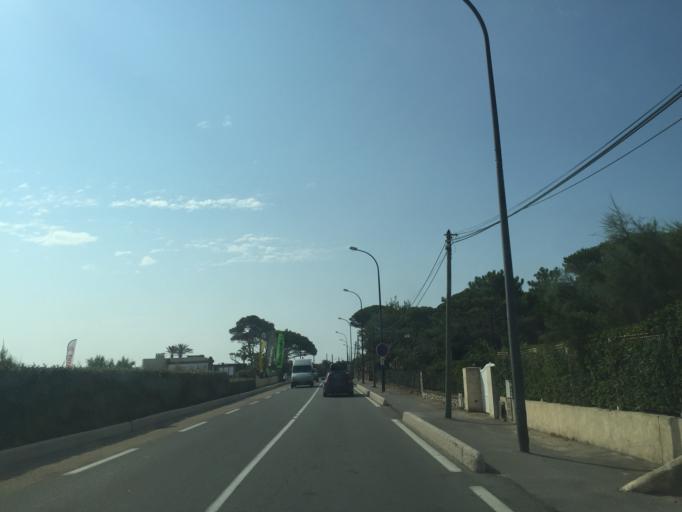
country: FR
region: Provence-Alpes-Cote d'Azur
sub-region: Departement du Var
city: Sainte-Maxime
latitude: 43.3174
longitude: 6.6662
